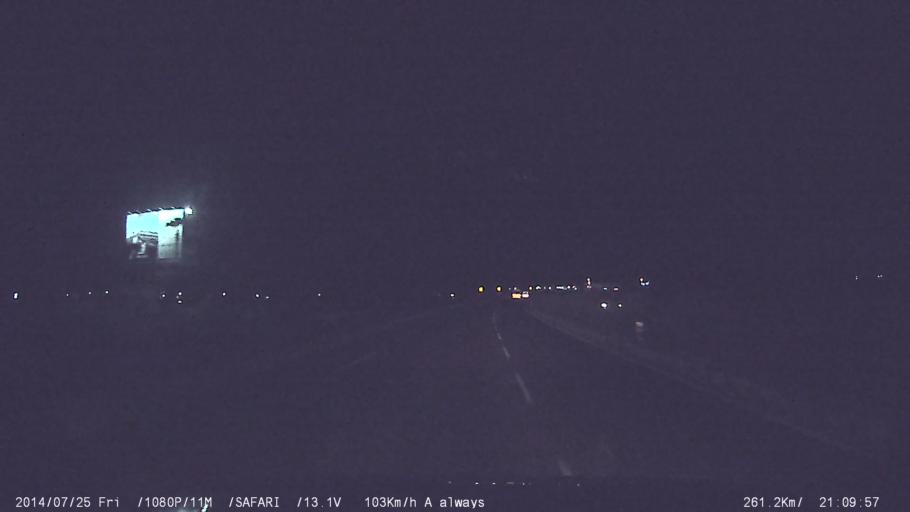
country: IN
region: Tamil Nadu
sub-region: Erode
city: Bhavani
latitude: 11.3861
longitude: 77.6544
